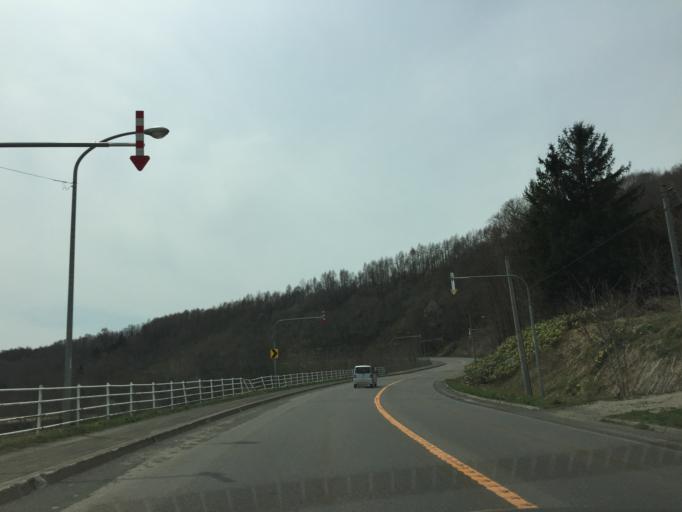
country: JP
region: Hokkaido
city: Ashibetsu
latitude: 43.5631
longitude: 142.1825
